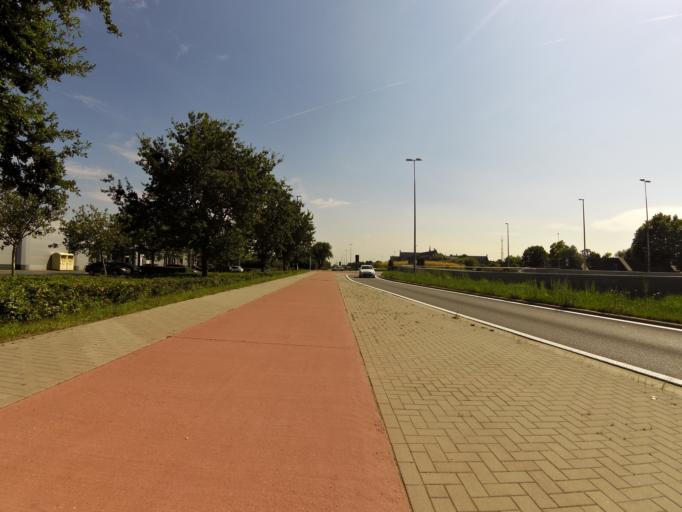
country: BE
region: Flanders
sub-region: Provincie West-Vlaanderen
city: Brugge
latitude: 51.2069
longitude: 3.1925
